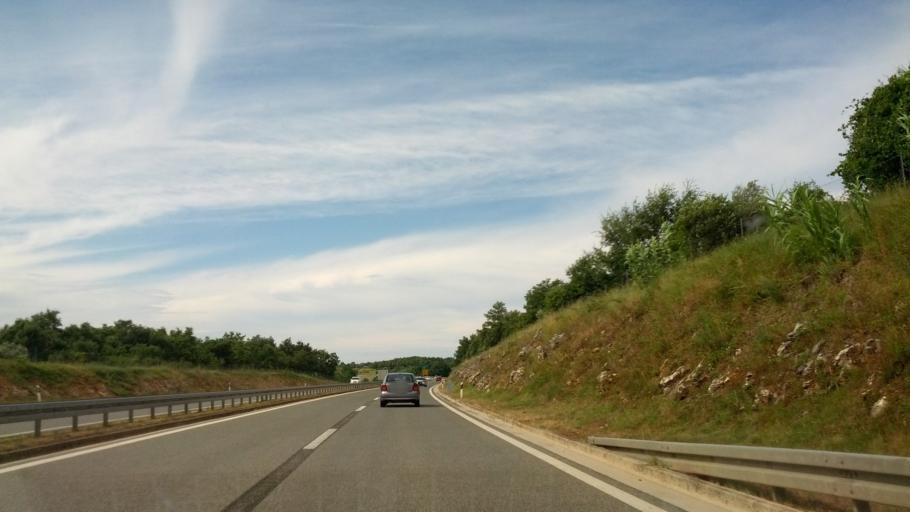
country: HR
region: Istarska
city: Buje
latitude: 45.3645
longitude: 13.6236
